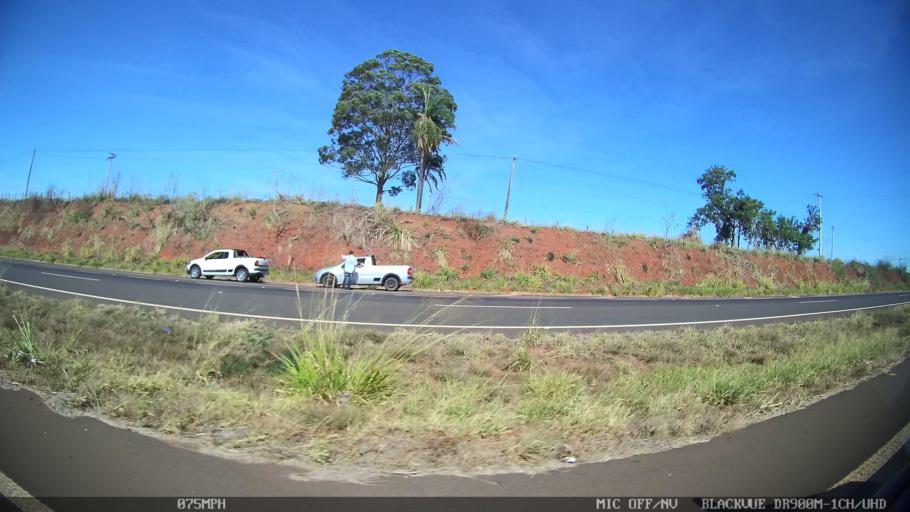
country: BR
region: Sao Paulo
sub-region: Barretos
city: Barretos
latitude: -20.5423
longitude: -48.6182
